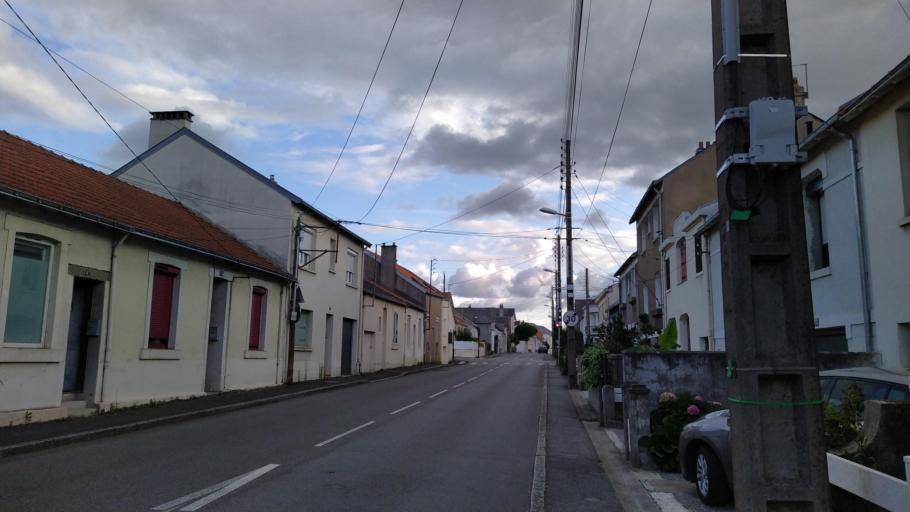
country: FR
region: Pays de la Loire
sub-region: Departement de la Loire-Atlantique
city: Nantes
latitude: 47.2382
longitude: -1.5388
